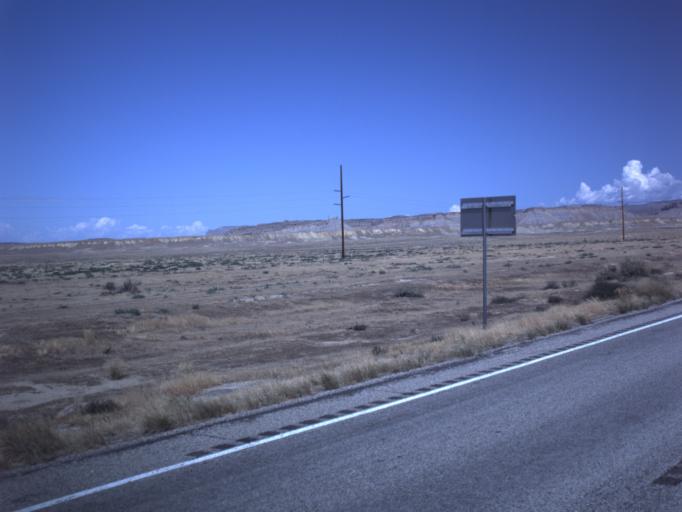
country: US
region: Utah
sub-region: Grand County
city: Moab
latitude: 38.9032
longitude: -109.8143
